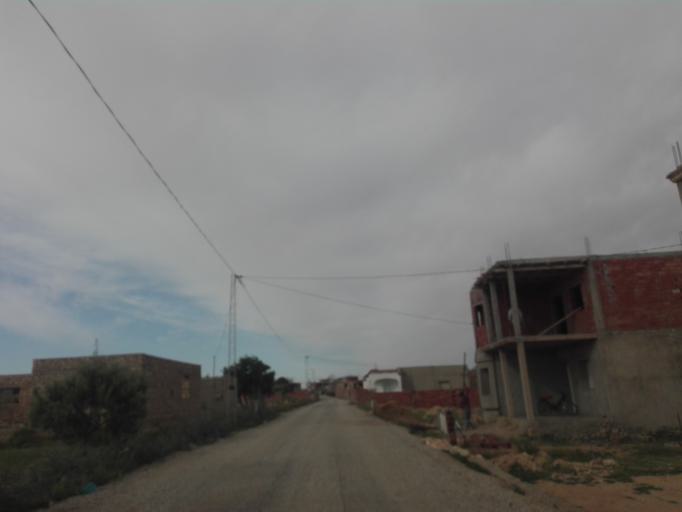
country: TN
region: Safaqis
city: Sfax
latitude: 34.7310
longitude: 10.4941
